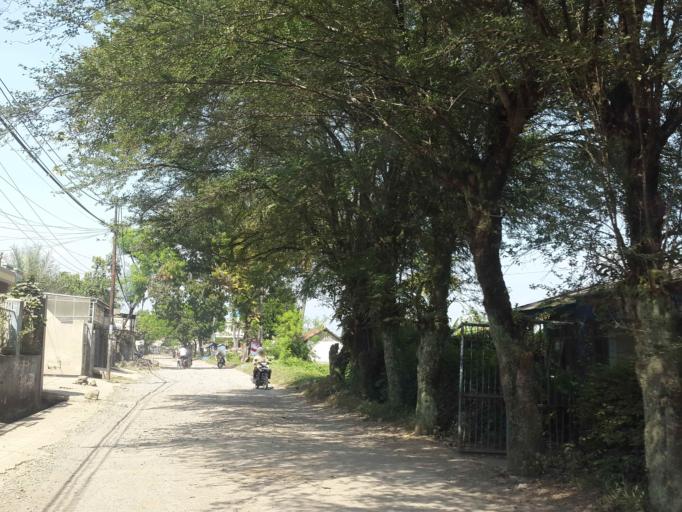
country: ID
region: West Java
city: Ciranjang-hilir
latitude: -6.8170
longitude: 107.2495
